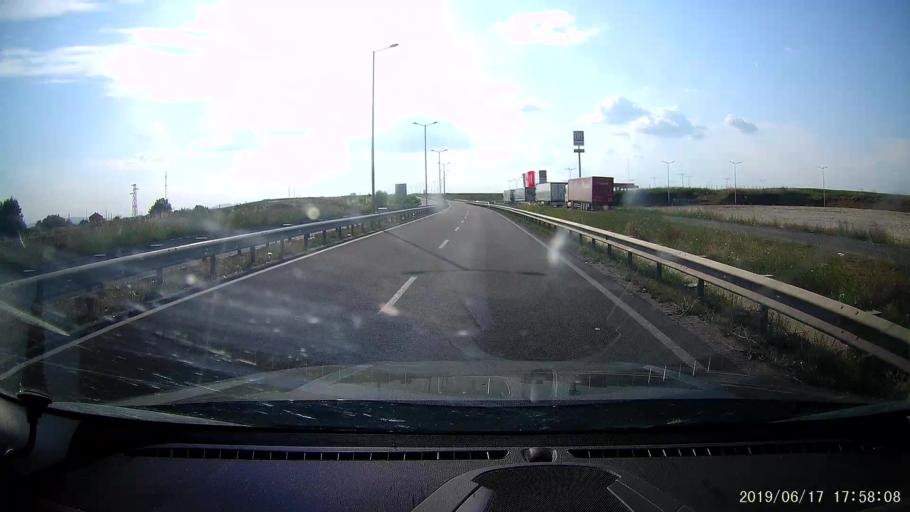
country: BG
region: Khaskovo
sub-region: Obshtina Svilengrad
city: Svilengrad
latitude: 41.7247
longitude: 26.3258
